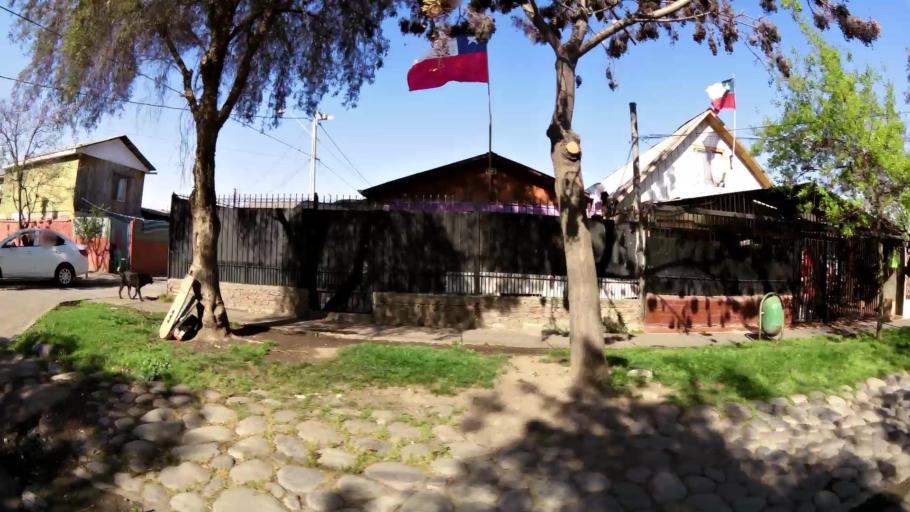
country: CL
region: Santiago Metropolitan
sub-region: Provincia de Santiago
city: La Pintana
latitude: -33.5837
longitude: -70.6502
